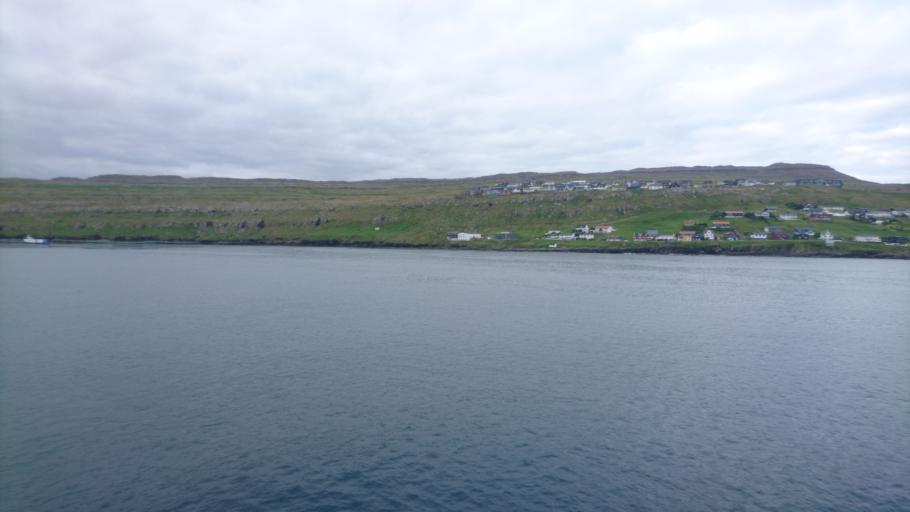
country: FO
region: Streymoy
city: Argir
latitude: 61.9966
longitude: -6.7569
